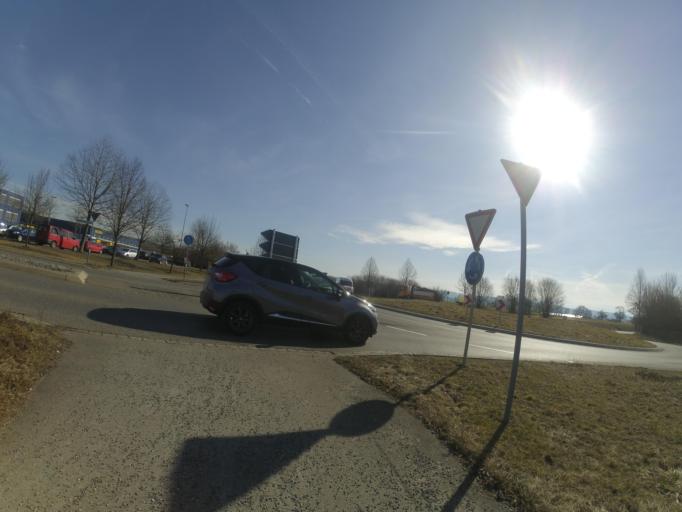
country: DE
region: Baden-Wuerttemberg
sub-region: Tuebingen Region
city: Baindt
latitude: 47.8469
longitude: 9.6407
